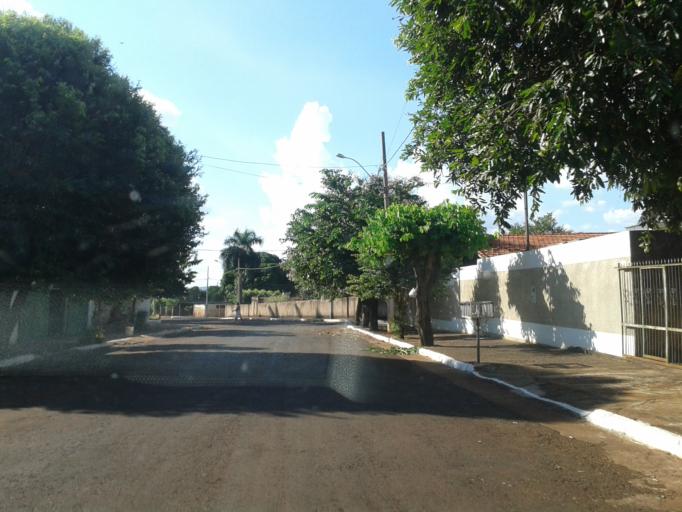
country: BR
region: Minas Gerais
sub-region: Capinopolis
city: Capinopolis
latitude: -18.5178
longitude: -49.5013
